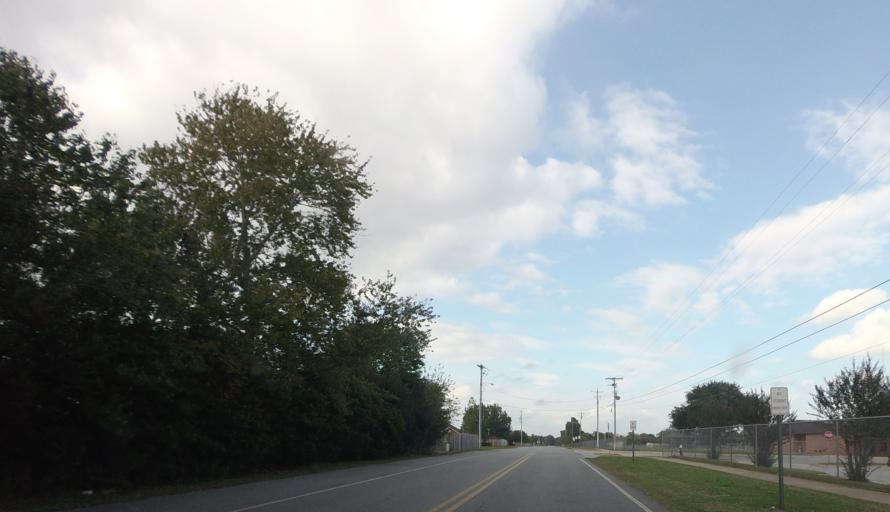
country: US
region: Georgia
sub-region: Houston County
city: Centerville
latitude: 32.6352
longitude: -83.6455
